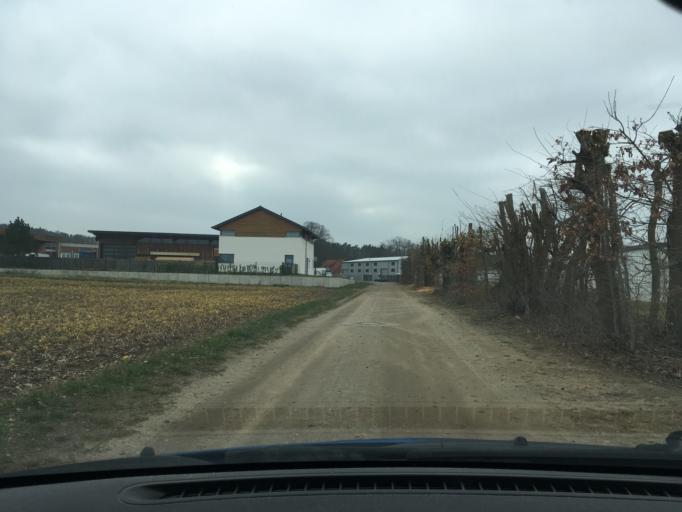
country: DE
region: Lower Saxony
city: Kirchgellersen
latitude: 53.2267
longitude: 10.2867
